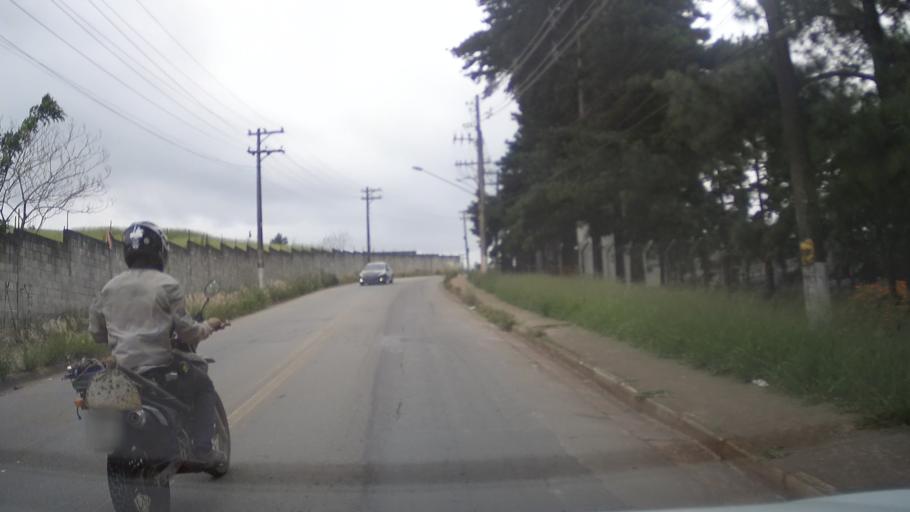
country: BR
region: Sao Paulo
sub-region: Itaquaquecetuba
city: Itaquaquecetuba
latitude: -23.4508
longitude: -46.3811
